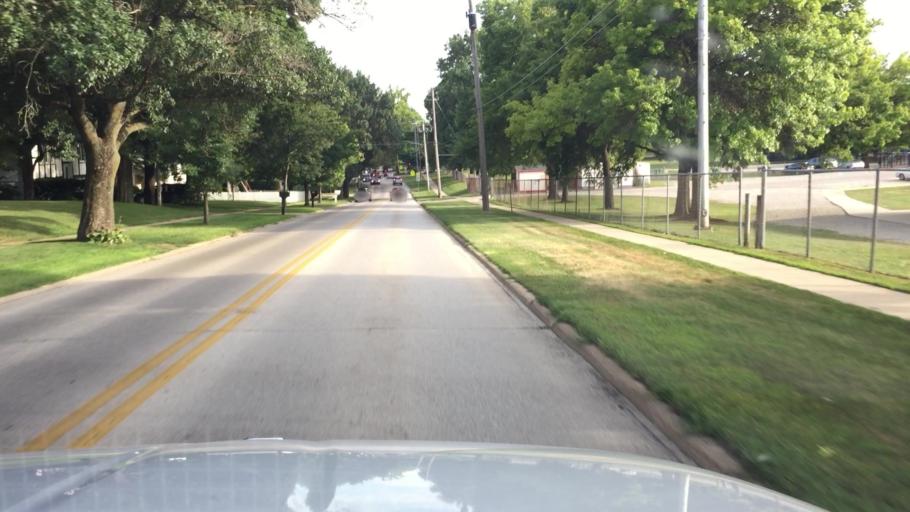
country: US
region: Iowa
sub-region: Johnson County
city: Iowa City
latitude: 41.6591
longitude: -91.5021
